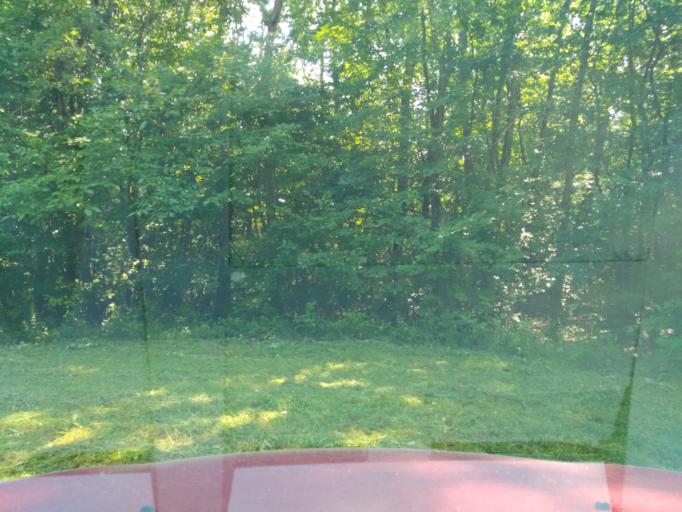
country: SK
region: Kosicky
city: Moldava nad Bodvou
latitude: 48.6183
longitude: 21.0421
